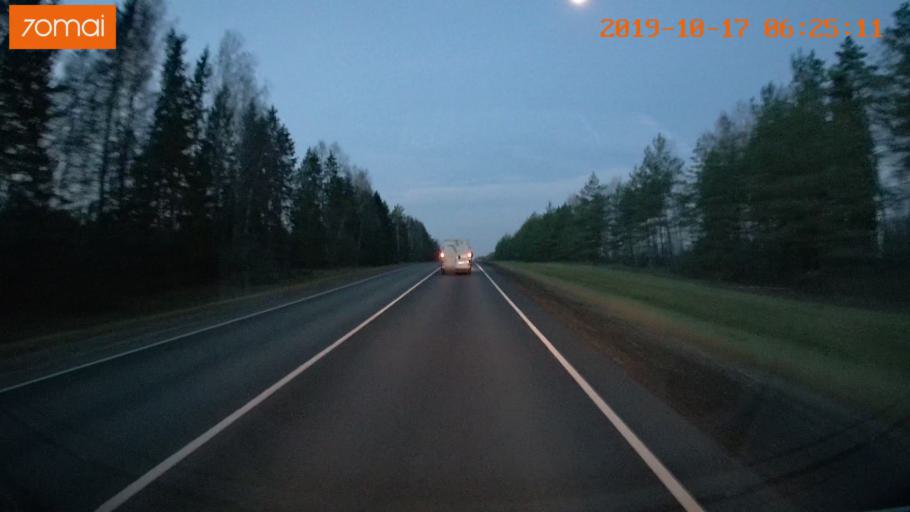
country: RU
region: Ivanovo
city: Lezhnevo
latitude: 56.7703
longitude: 40.8120
